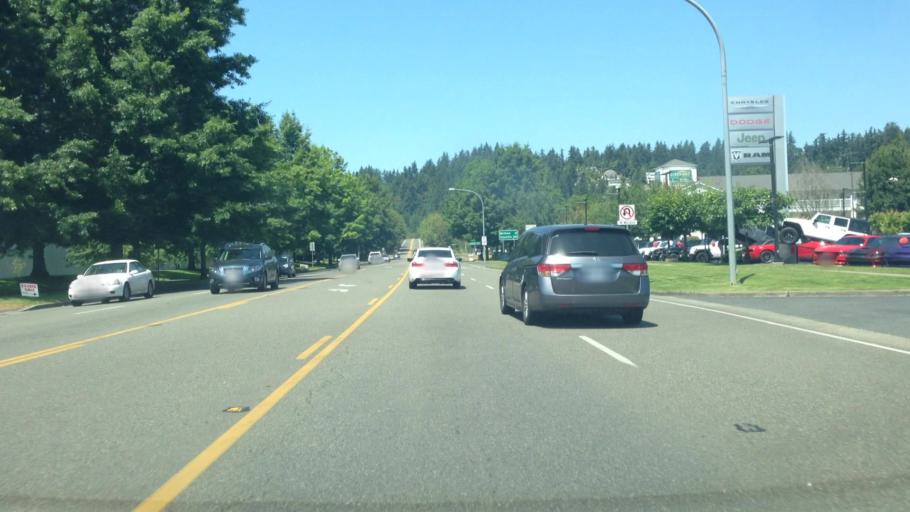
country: US
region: Washington
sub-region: Pierce County
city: North Puyallup
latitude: 47.2077
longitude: -122.2938
